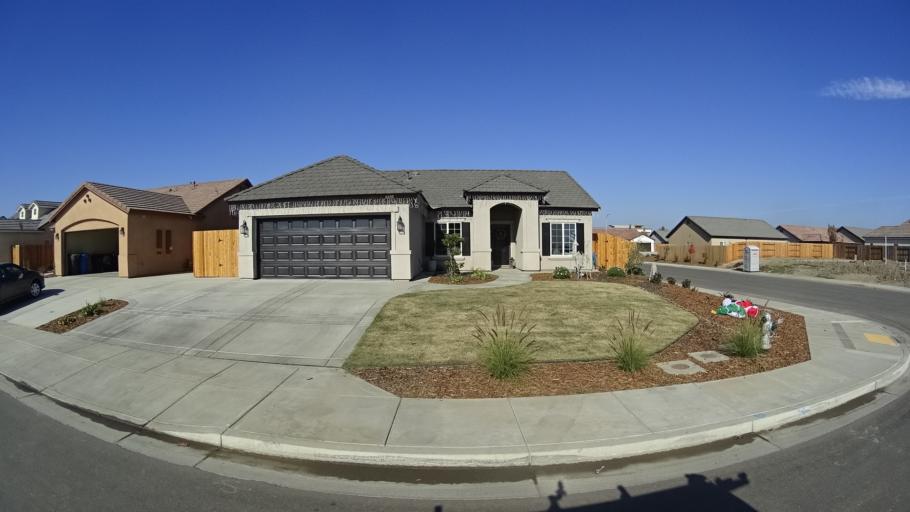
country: US
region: California
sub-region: Kern County
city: Greenfield
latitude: 35.2932
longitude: -119.0761
